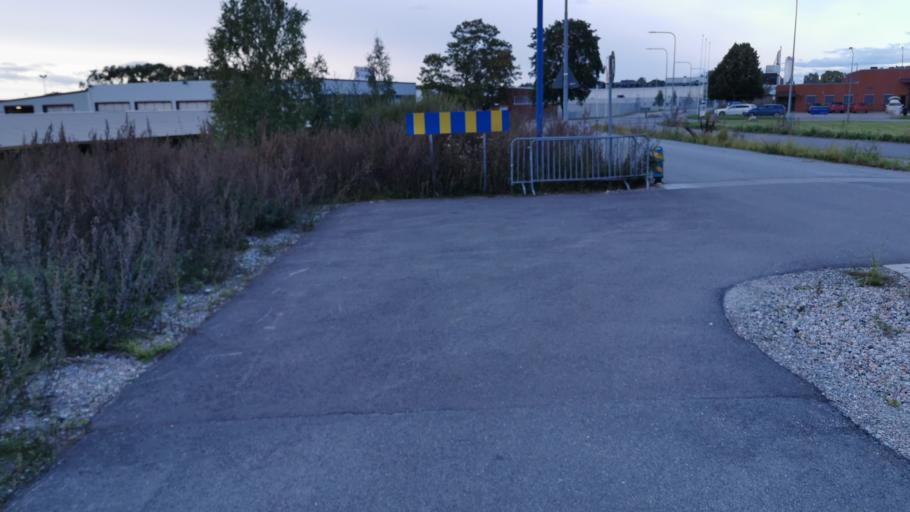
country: SE
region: OErebro
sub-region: Orebro Kommun
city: Orebro
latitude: 59.3079
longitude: 15.2258
